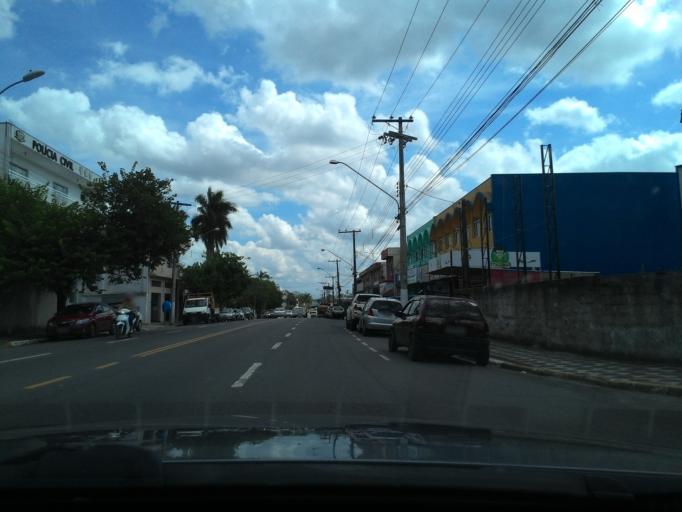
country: BR
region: Sao Paulo
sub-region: Registro
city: Registro
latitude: -24.4997
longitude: -47.8519
